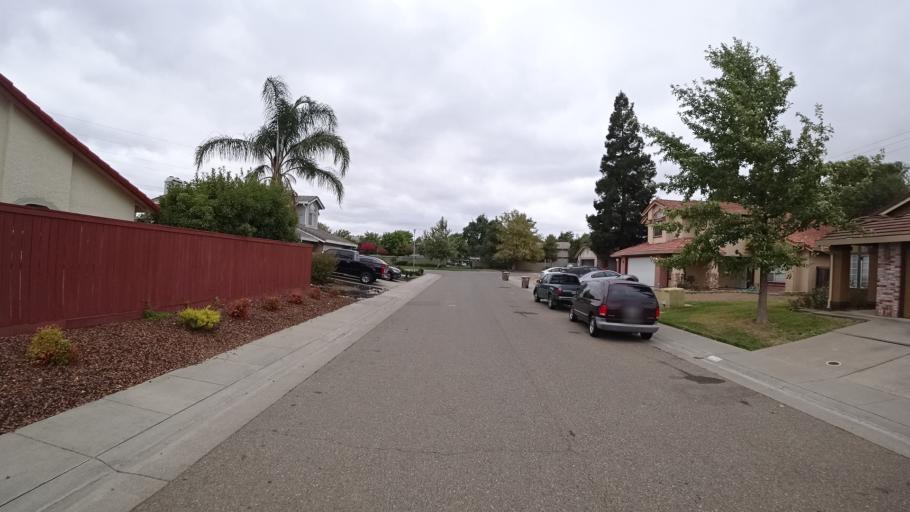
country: US
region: California
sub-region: Sacramento County
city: Laguna
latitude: 38.4191
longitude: -121.4493
